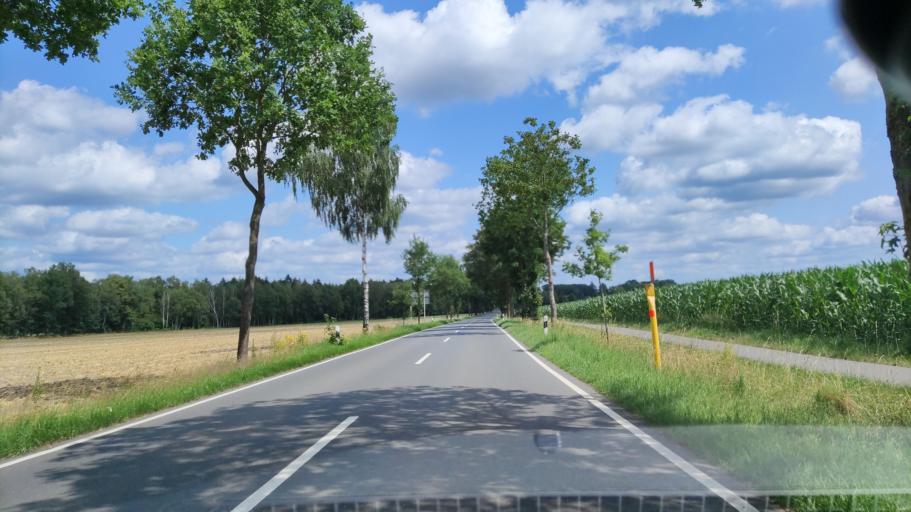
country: DE
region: Lower Saxony
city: Walsrode
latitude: 52.9085
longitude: 9.5766
